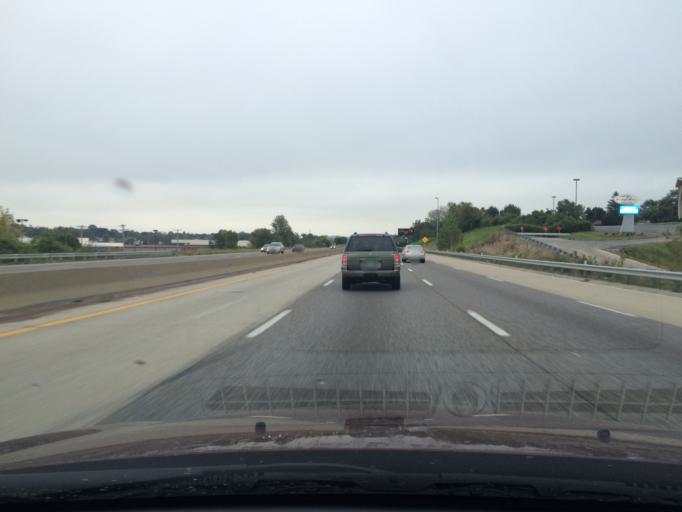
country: US
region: Missouri
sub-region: Saint Louis County
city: Bridgeton
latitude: 38.7454
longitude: -90.4291
